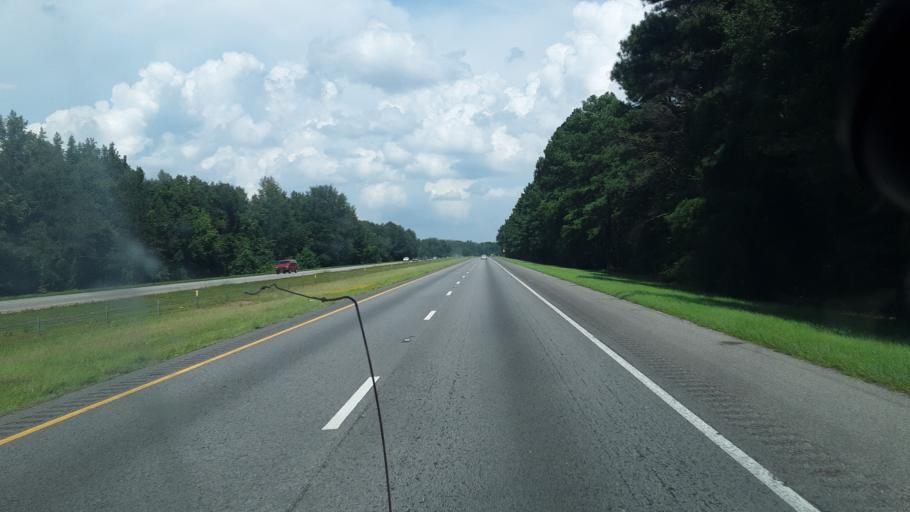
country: US
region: South Carolina
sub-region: Kershaw County
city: Lugoff
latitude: 34.2086
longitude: -80.6488
